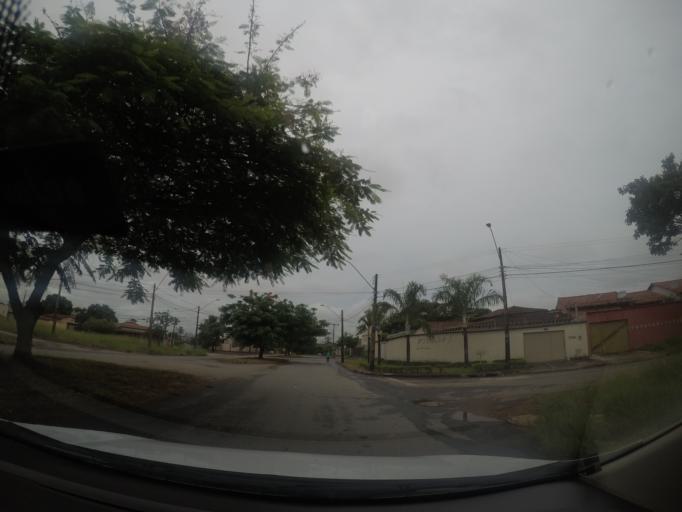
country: BR
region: Goias
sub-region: Goiania
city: Goiania
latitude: -16.7436
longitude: -49.3277
